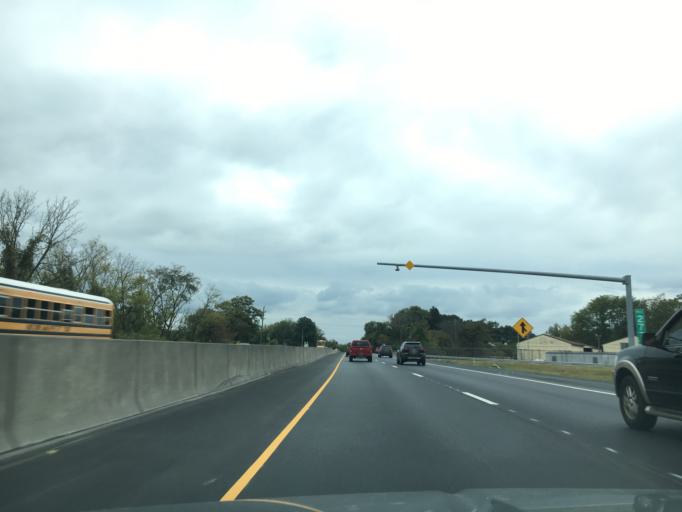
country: US
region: Pennsylvania
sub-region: Chester County
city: Downingtown
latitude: 40.0135
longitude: -75.7239
